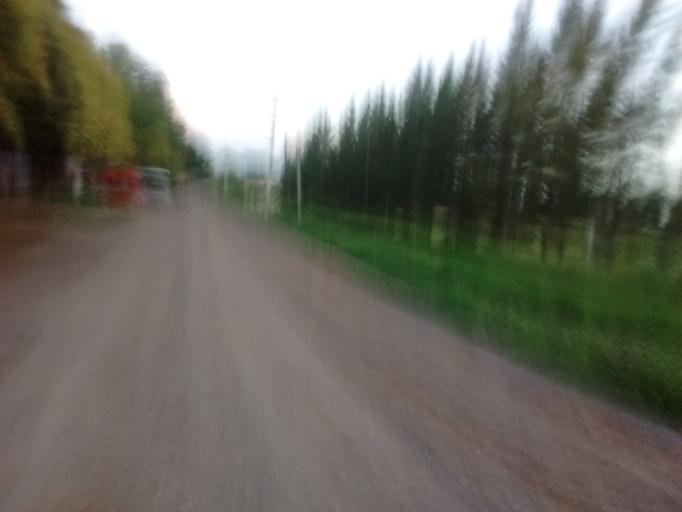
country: AR
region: Santa Fe
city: Funes
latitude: -32.9107
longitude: -60.8082
